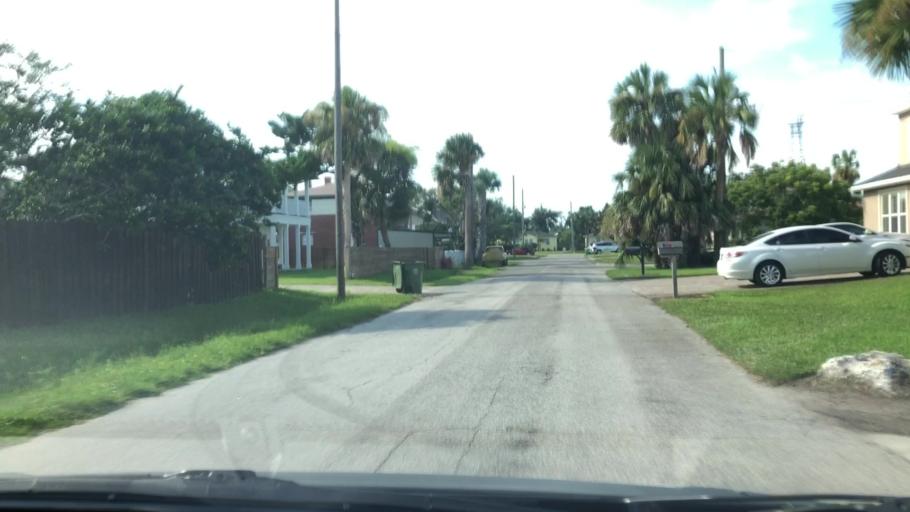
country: US
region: Florida
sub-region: Duval County
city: Jacksonville Beach
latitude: 30.3004
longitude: -81.3966
